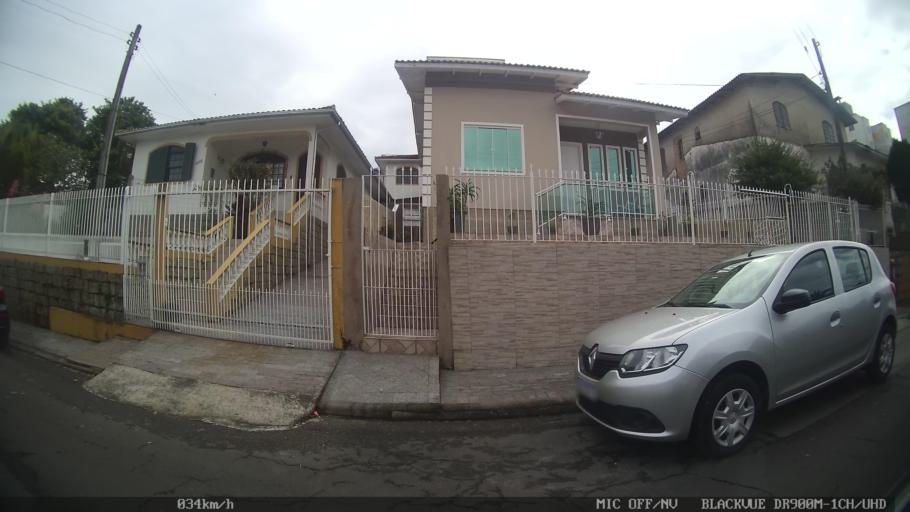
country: BR
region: Santa Catarina
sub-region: Sao Jose
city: Campinas
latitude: -27.5820
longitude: -48.6058
